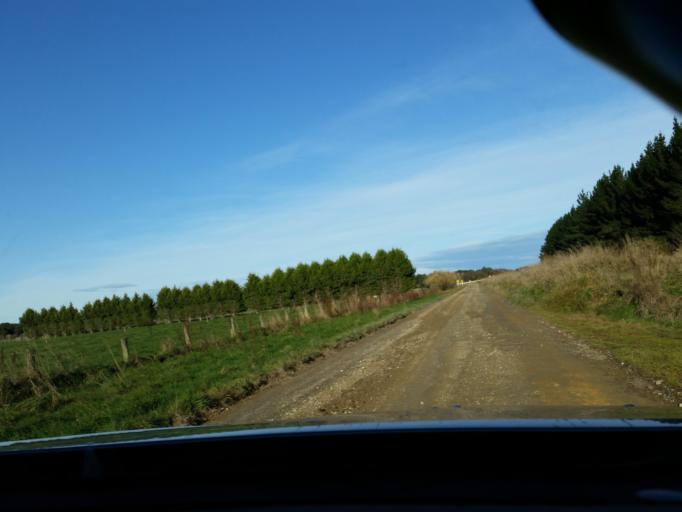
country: NZ
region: Southland
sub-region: Southland District
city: Winton
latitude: -46.2382
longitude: 168.4806
